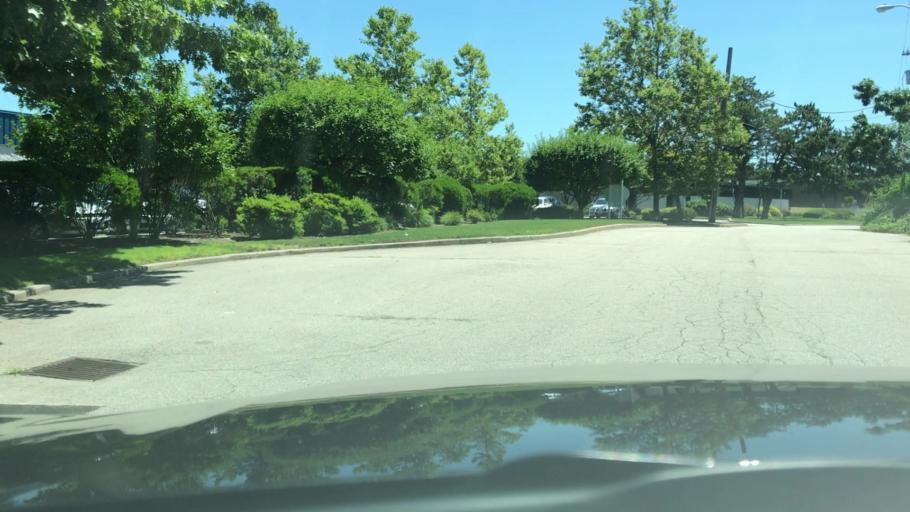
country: US
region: Rhode Island
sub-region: Providence County
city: Cranston
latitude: 41.7555
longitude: -71.4344
